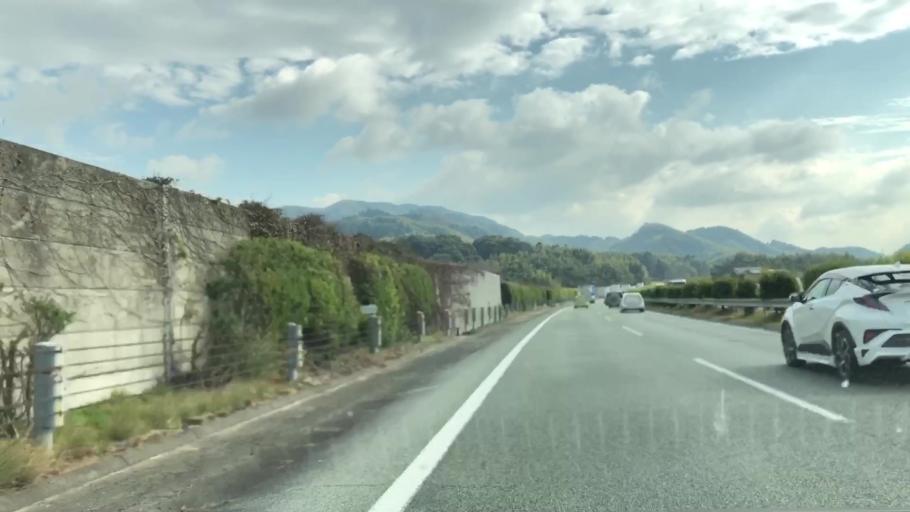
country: JP
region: Fukuoka
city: Setakamachi-takayanagi
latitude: 33.1152
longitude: 130.5287
